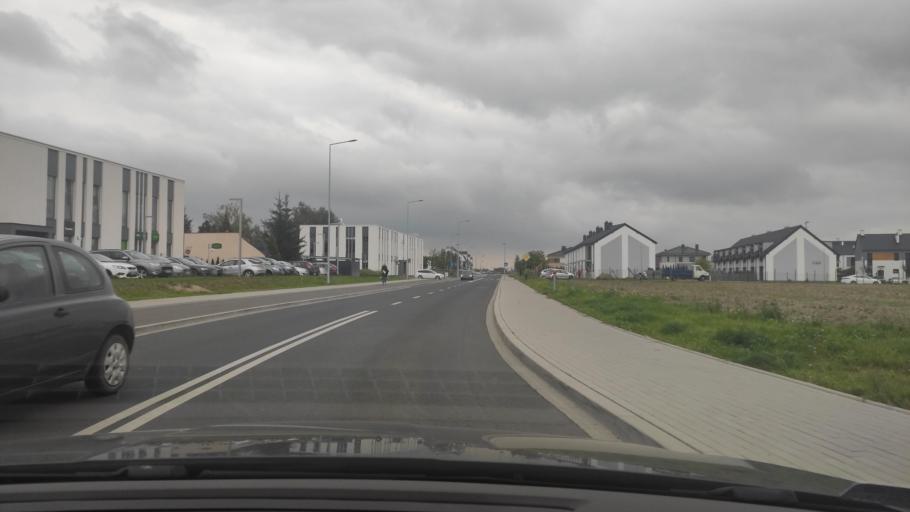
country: PL
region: Greater Poland Voivodeship
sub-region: Powiat poznanski
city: Swarzedz
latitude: 52.3896
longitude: 17.0697
